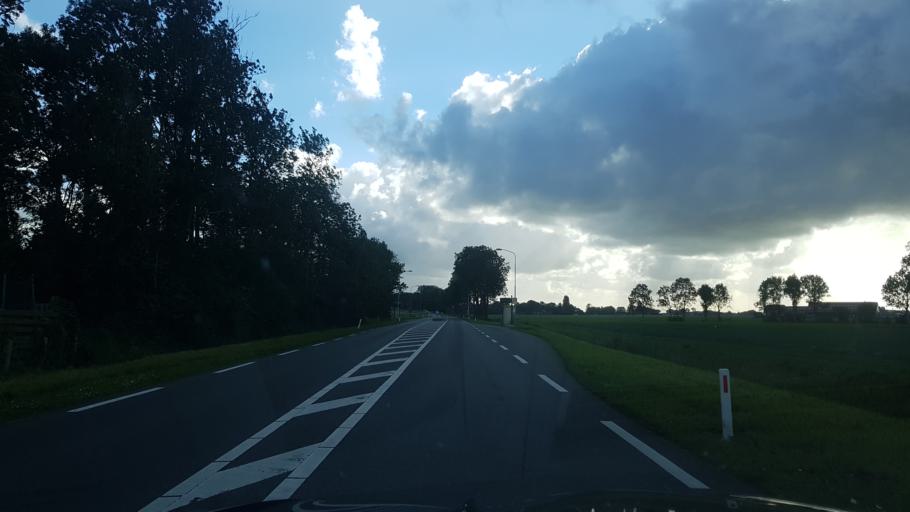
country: NL
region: Groningen
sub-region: Gemeente Appingedam
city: Appingedam
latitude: 53.3118
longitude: 6.7605
